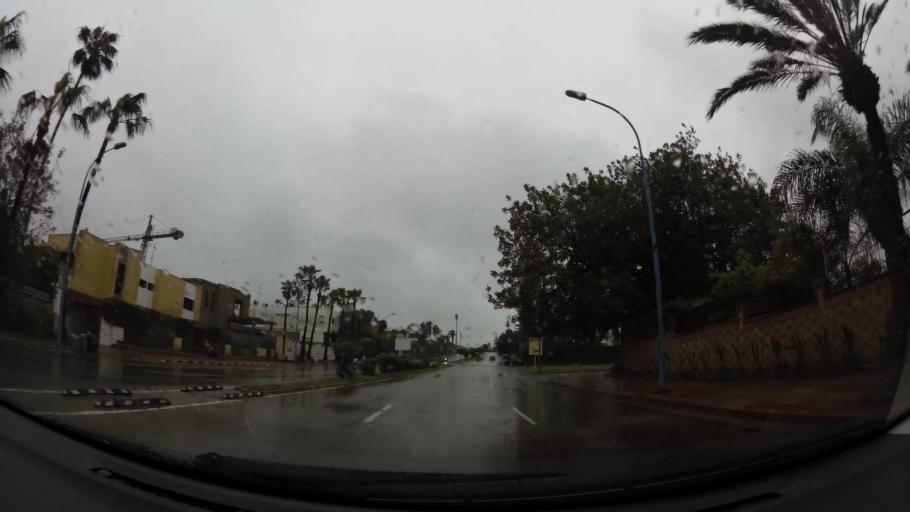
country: MA
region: Grand Casablanca
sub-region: Casablanca
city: Casablanca
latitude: 33.5877
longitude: -7.6731
